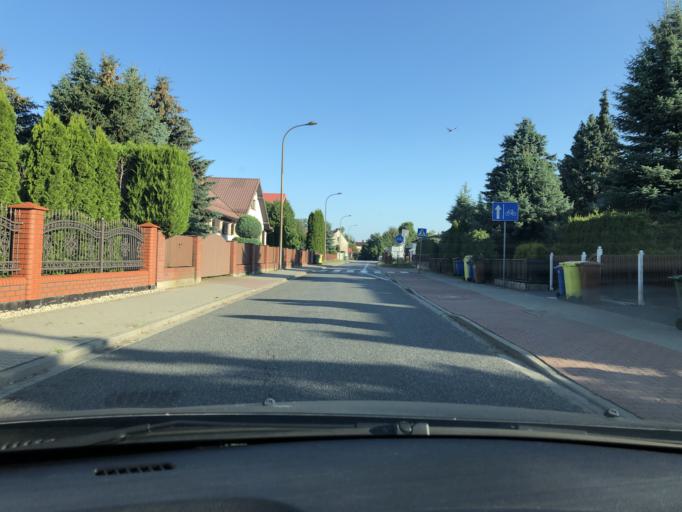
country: PL
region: Lodz Voivodeship
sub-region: Powiat wieruszowski
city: Wieruszow
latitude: 51.2922
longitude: 18.1607
